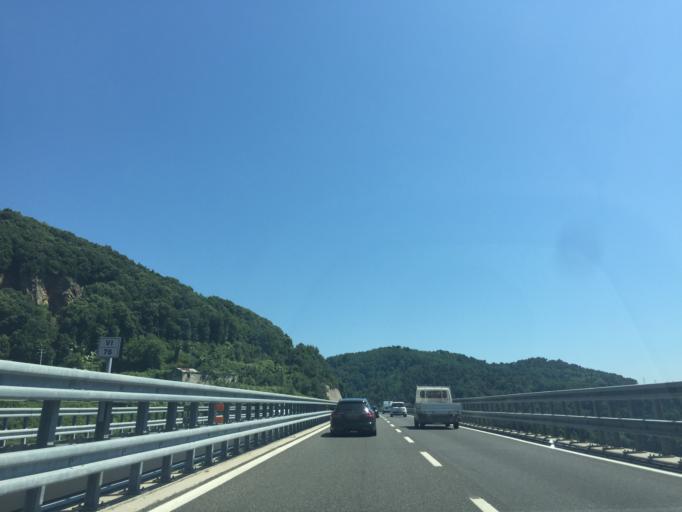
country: IT
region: Tuscany
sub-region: Provincia di Lucca
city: Massarosa
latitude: 43.8577
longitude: 10.3696
